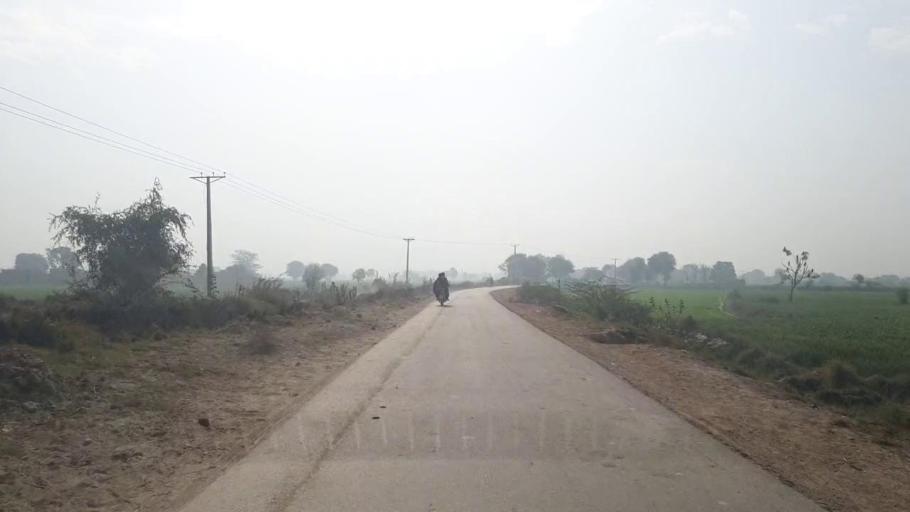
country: PK
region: Sindh
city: Hala
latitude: 25.7642
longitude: 68.4477
